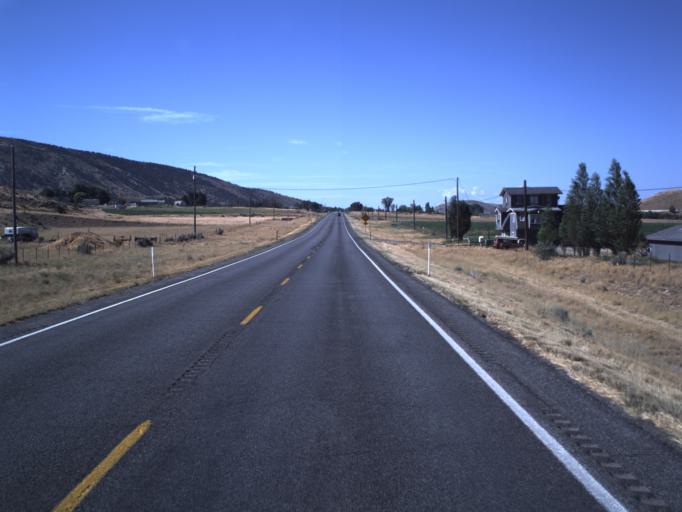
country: US
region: Utah
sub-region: Sanpete County
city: Manti
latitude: 39.2059
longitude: -111.6907
